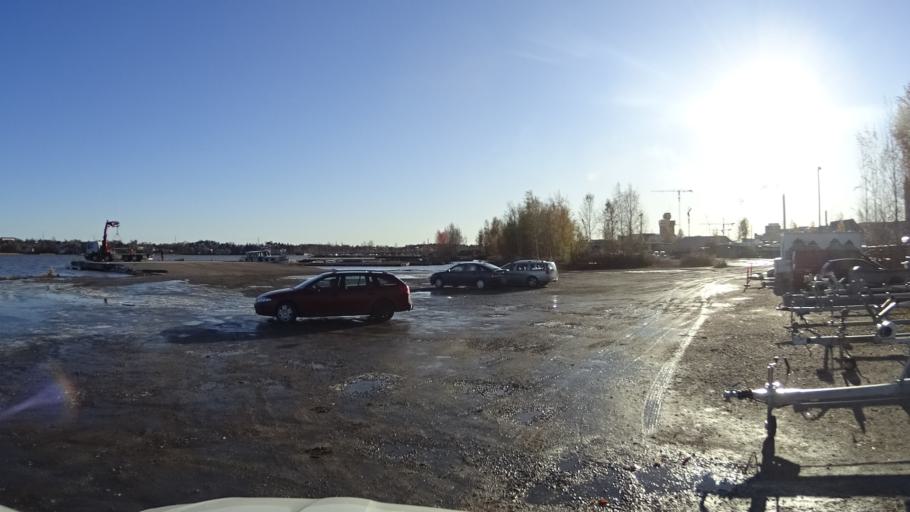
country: FI
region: Uusimaa
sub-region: Helsinki
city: Helsinki
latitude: 60.1962
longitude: 24.9844
